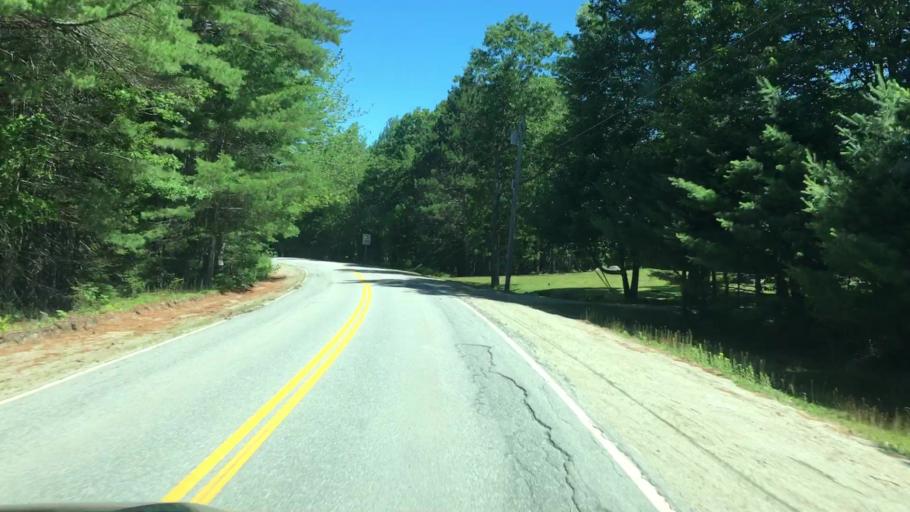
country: US
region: Maine
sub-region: Hancock County
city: Penobscot
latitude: 44.4465
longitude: -68.7019
